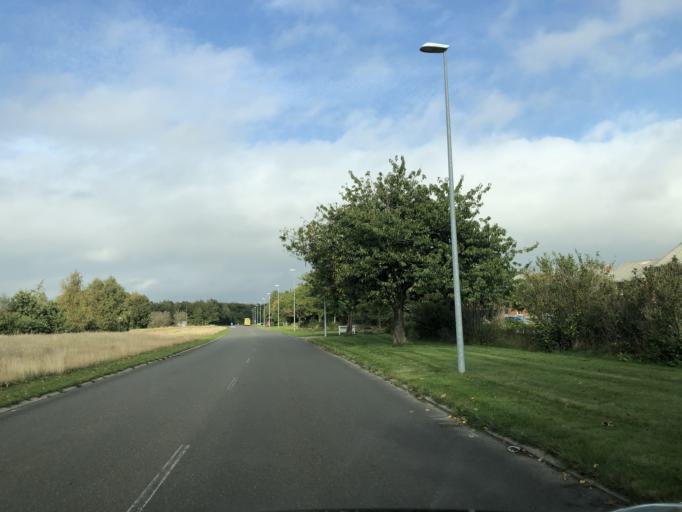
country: DK
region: Central Jutland
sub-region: Holstebro Kommune
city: Holstebro
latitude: 56.3709
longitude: 8.5906
